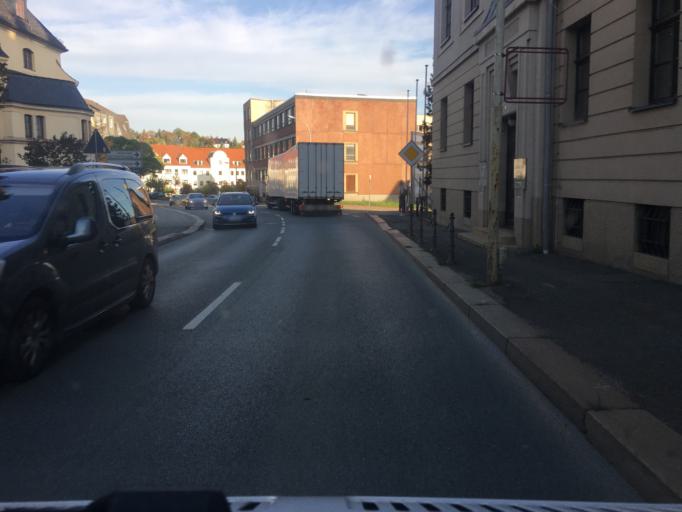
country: DE
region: Saxony
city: Werdau
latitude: 50.7373
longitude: 12.3776
